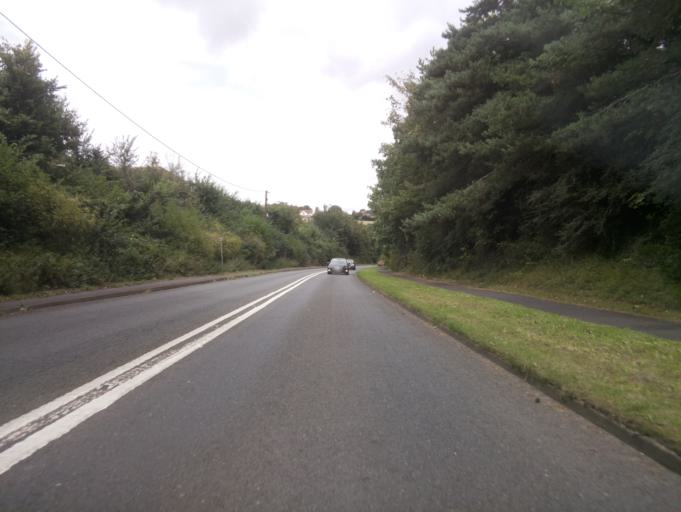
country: GB
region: England
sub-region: Devon
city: Dawlish
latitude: 50.5665
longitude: -3.4761
